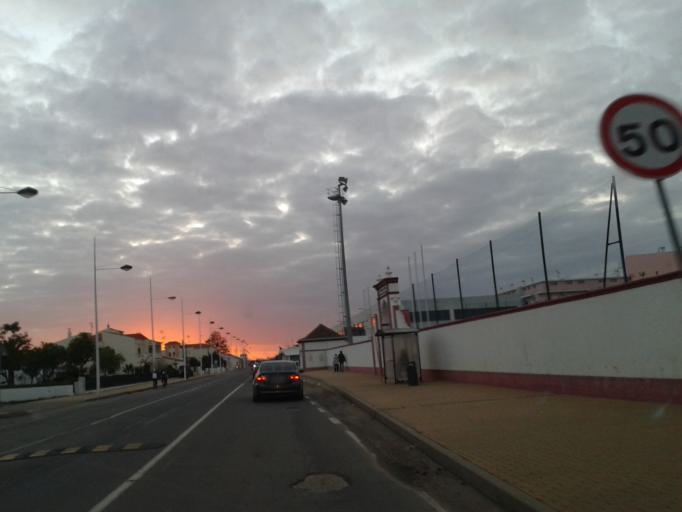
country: PT
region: Faro
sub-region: Vila Real de Santo Antonio
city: Vila Real de Santo Antonio
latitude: 37.1928
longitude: -7.4251
